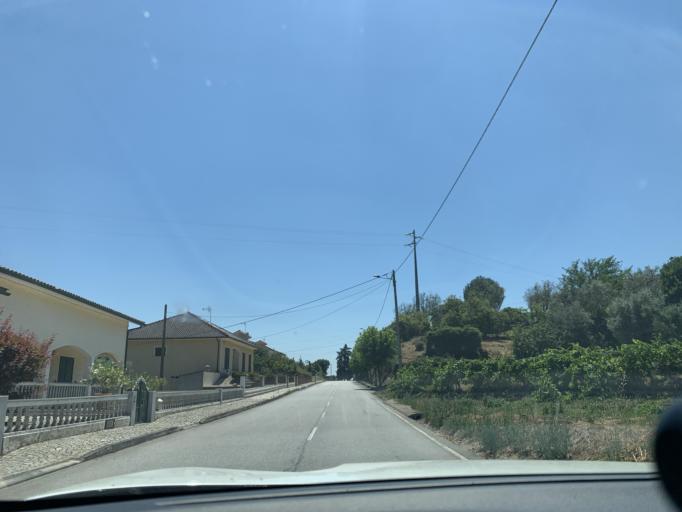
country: PT
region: Guarda
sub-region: Fornos de Algodres
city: Fornos de Algodres
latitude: 40.5776
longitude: -7.6420
